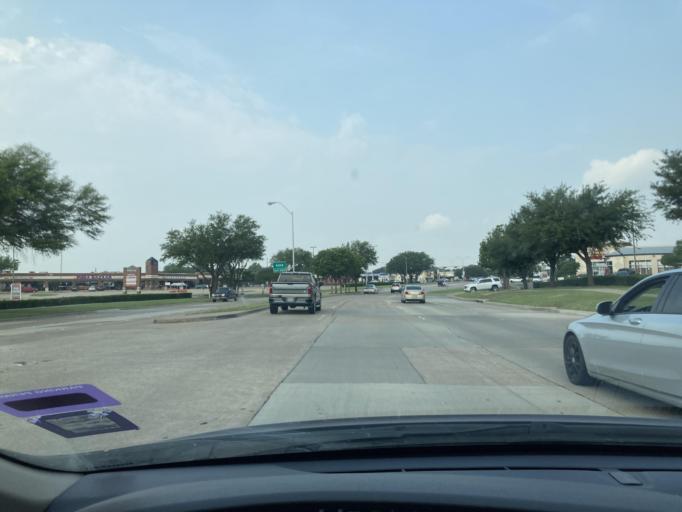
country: US
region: Texas
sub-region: Collin County
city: Plano
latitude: 33.0570
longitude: -96.7075
